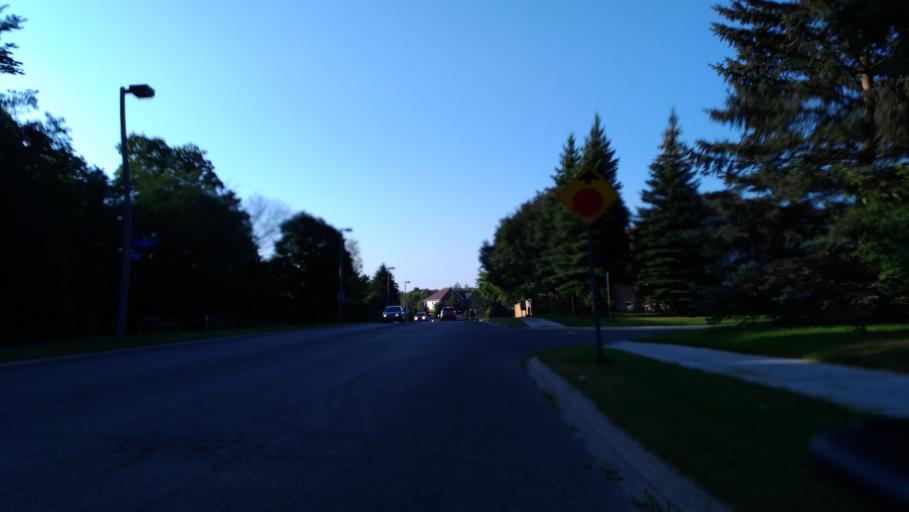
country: CA
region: Ontario
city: Bells Corners
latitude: 45.3472
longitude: -75.9322
